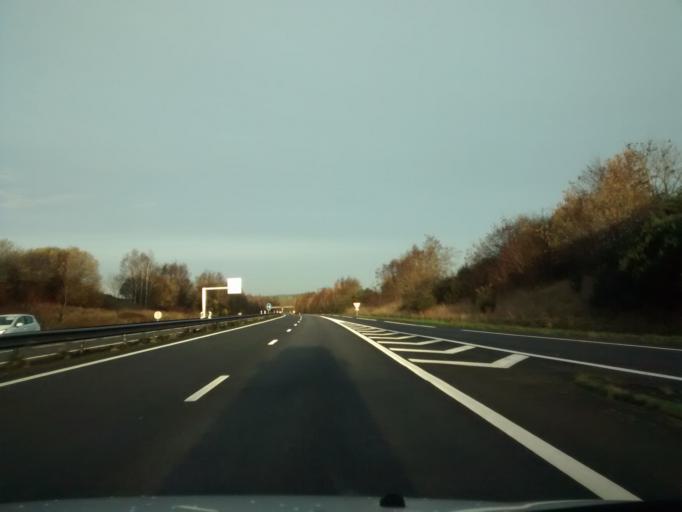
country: FR
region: Brittany
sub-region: Departement d'Ille-et-Vilaine
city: Saint-Domineuc
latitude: 48.3658
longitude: -1.8780
